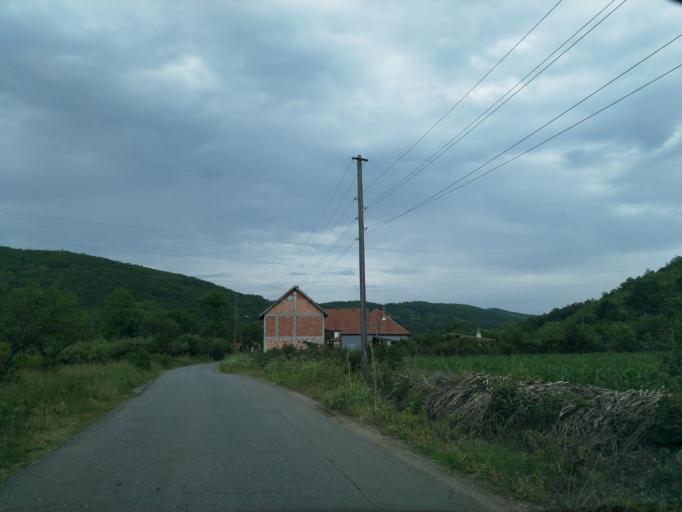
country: RS
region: Central Serbia
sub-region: Borski Okrug
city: Bor
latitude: 44.0266
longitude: 21.9727
